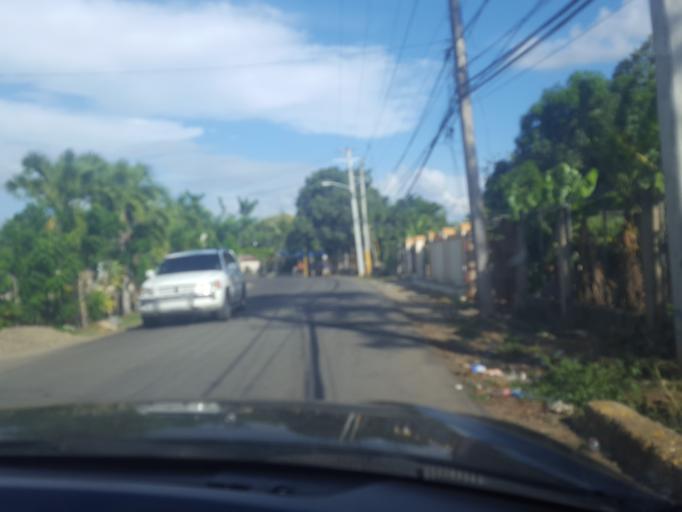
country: DO
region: La Vega
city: Rio Verde Arriba
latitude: 19.3447
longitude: -70.6207
